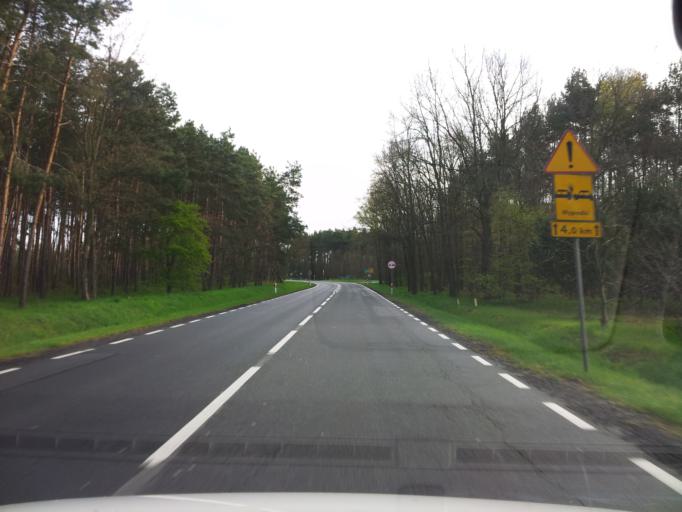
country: PL
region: Lubusz
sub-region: Powiat zielonogorski
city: Swidnica
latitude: 51.8802
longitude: 15.3779
